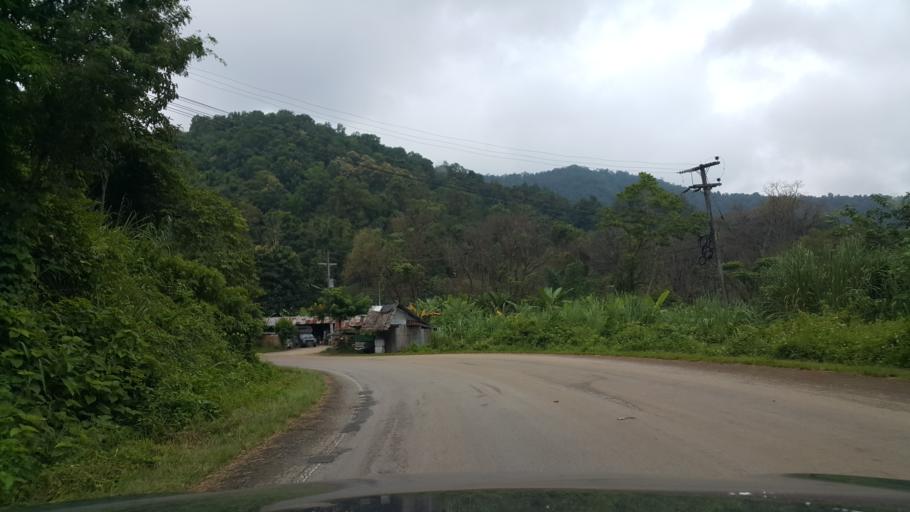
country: TH
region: Chiang Mai
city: Samoeng
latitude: 18.8096
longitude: 98.8208
